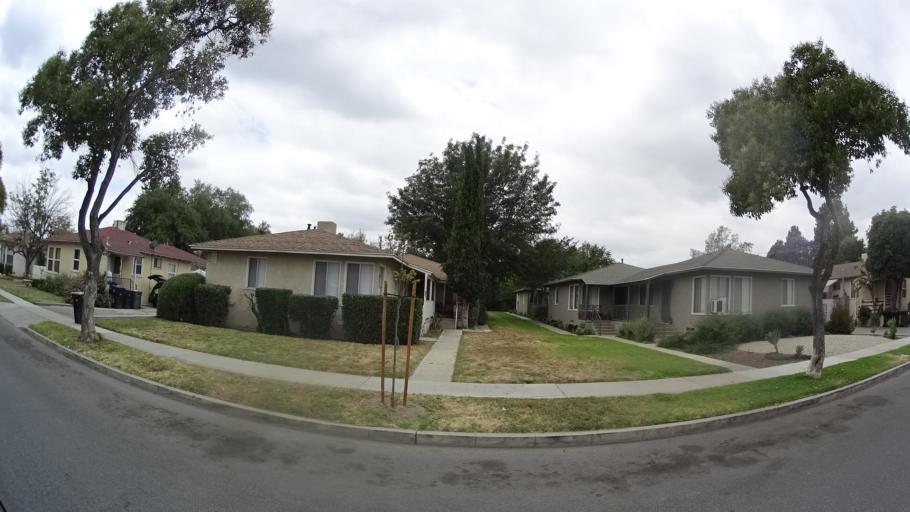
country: US
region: California
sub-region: Los Angeles County
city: Universal City
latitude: 34.1652
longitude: -118.3394
